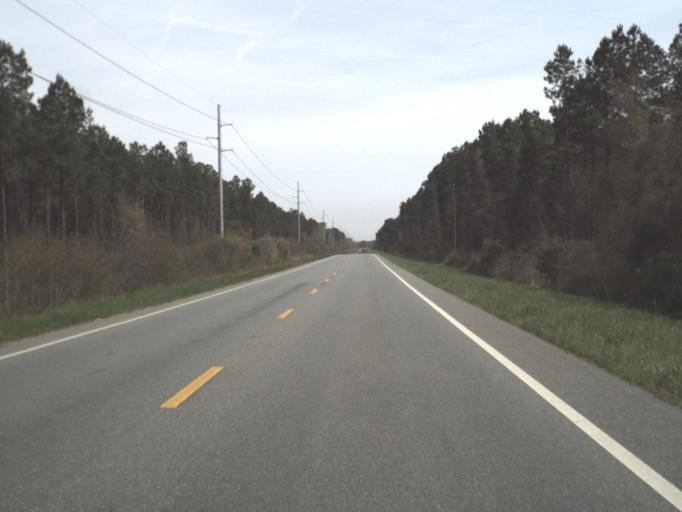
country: US
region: Alabama
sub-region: Houston County
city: Cottonwood
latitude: 30.9450
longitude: -85.3504
